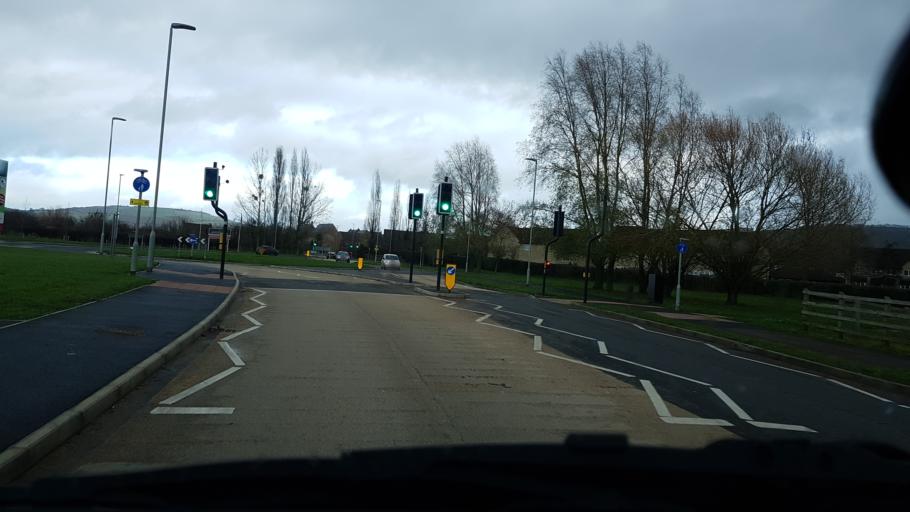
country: GB
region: England
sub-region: Gloucestershire
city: Gotherington
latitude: 51.9509
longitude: -2.0691
